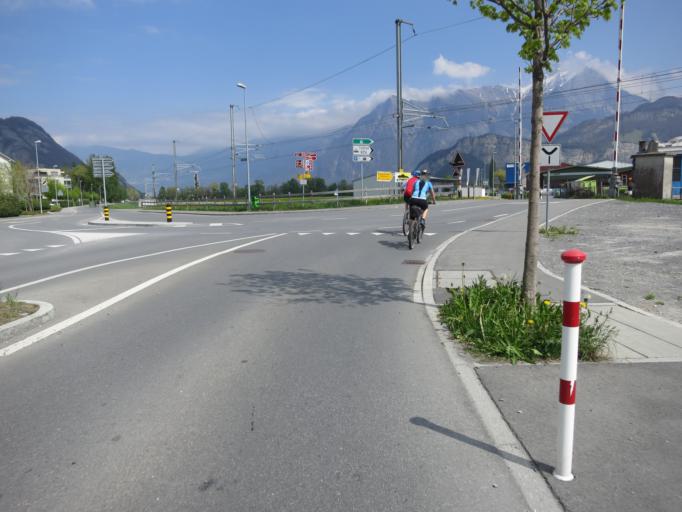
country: CH
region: Saint Gallen
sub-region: Wahlkreis Sarganserland
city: Sargans
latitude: 47.0496
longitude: 9.4455
